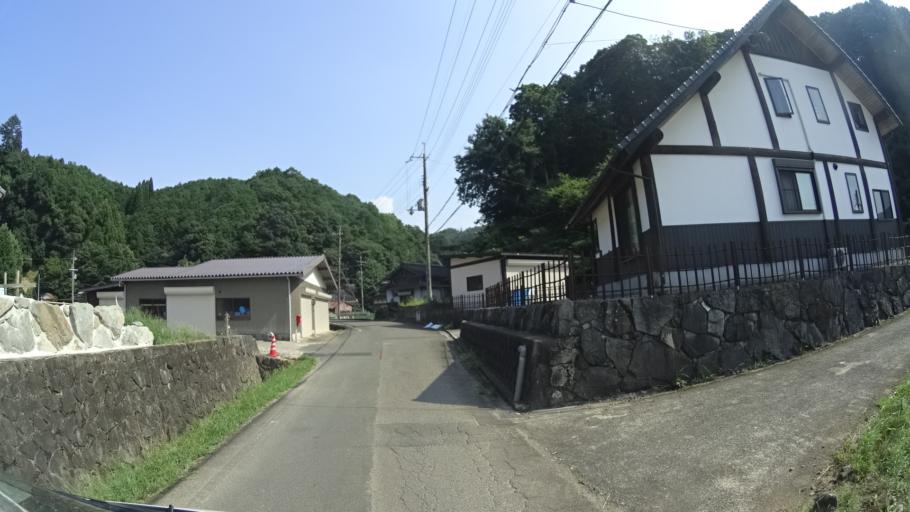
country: JP
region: Kyoto
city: Maizuru
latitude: 35.4232
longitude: 135.2217
